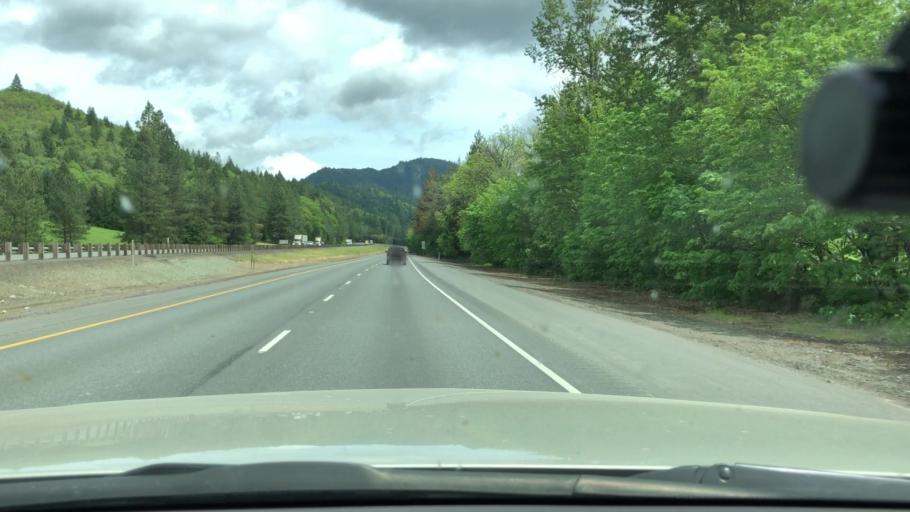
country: US
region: Oregon
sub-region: Josephine County
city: Merlin
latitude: 42.7023
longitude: -123.3769
